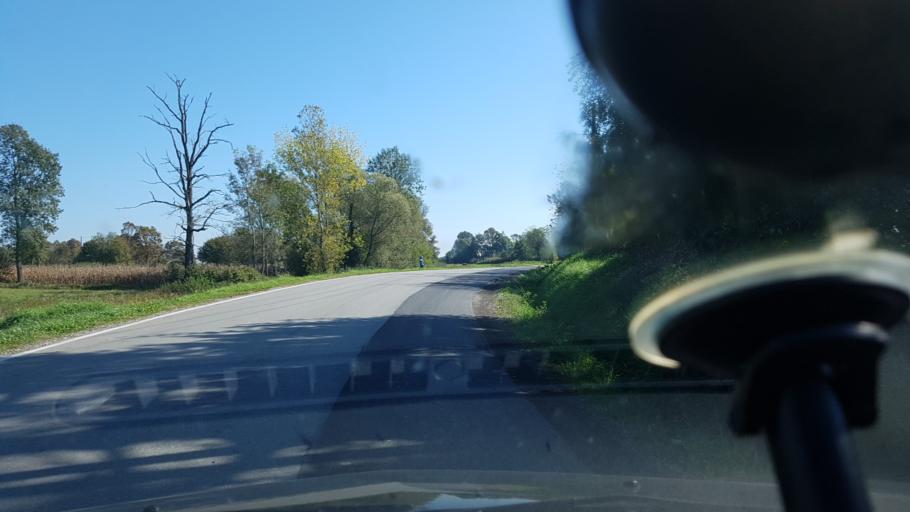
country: HR
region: Zagrebacka
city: Lupoglav
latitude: 45.7051
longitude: 16.3457
